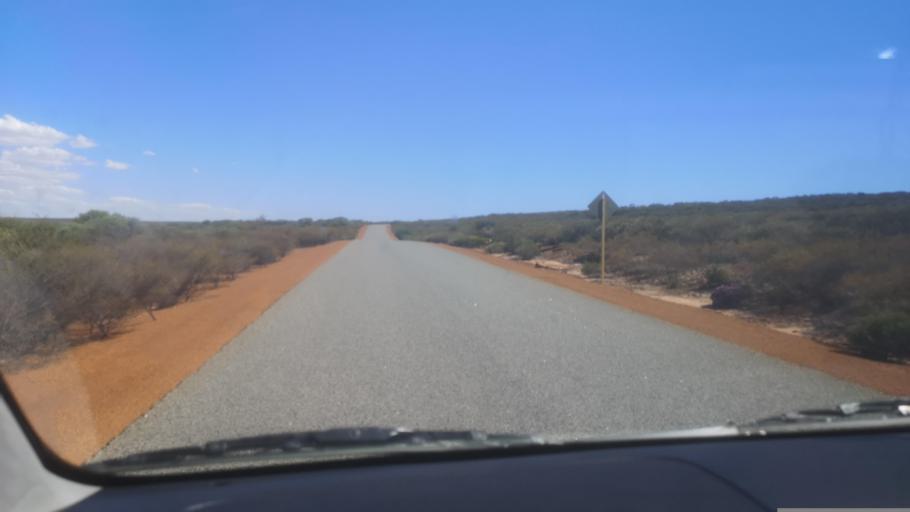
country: AU
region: Western Australia
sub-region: Northampton Shire
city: Kalbarri
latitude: -27.8130
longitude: 114.4706
